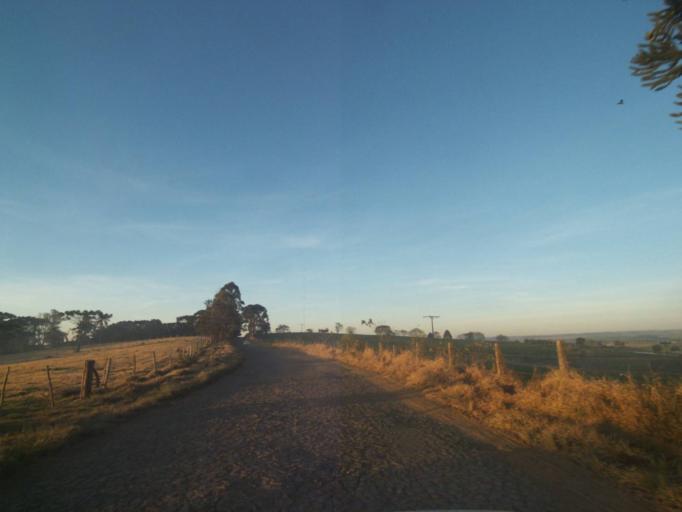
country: BR
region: Parana
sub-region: Tibagi
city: Tibagi
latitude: -24.5328
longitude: -50.4598
